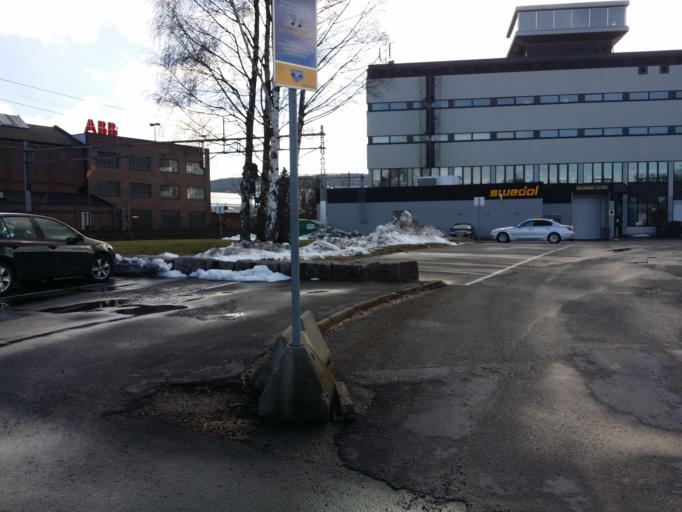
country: NO
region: Buskerud
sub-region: Drammen
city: Drammen
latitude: 59.7437
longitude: 10.2320
